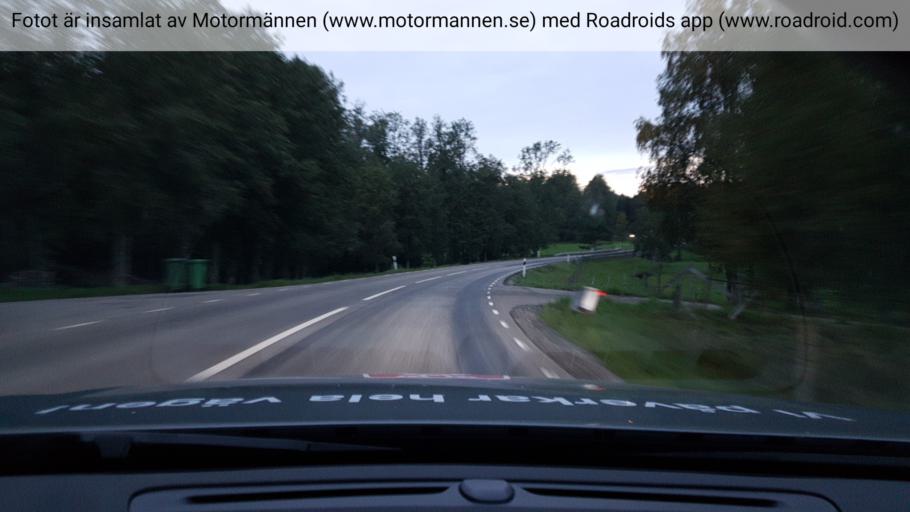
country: SE
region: OErebro
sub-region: Nora Kommun
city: As
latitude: 59.4600
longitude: 14.8679
